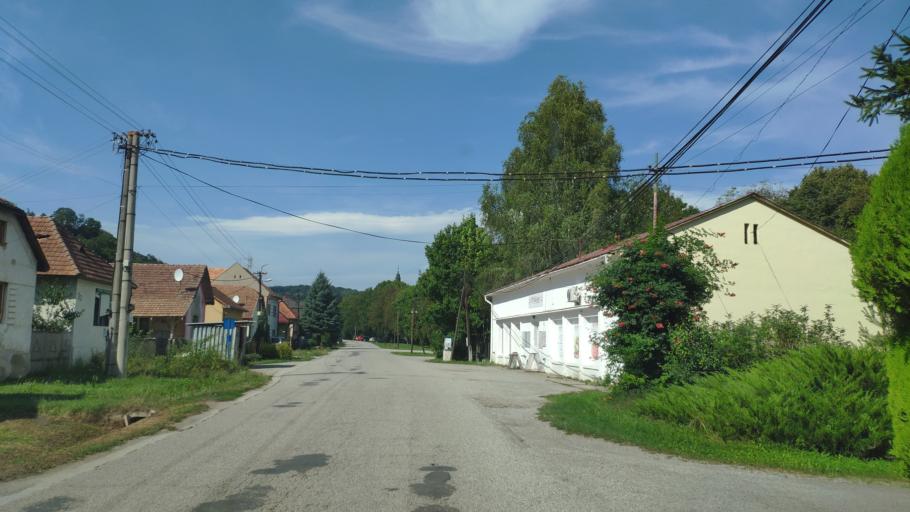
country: HU
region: Borsod-Abauj-Zemplen
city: Putnok
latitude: 48.4458
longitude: 20.3159
